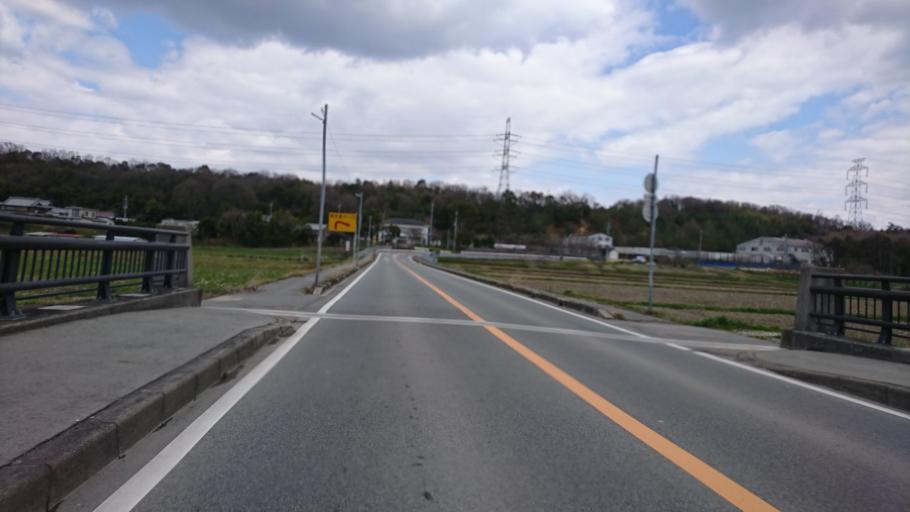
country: JP
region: Hyogo
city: Miki
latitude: 34.7665
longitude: 134.9527
